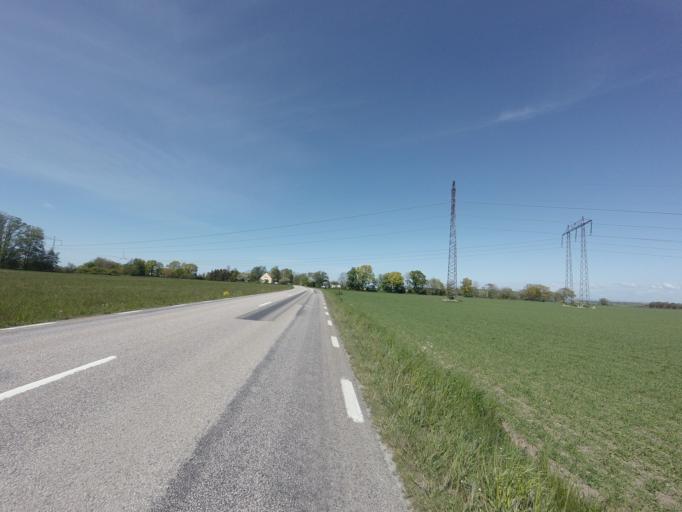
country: SE
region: Skane
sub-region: Helsingborg
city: Odakra
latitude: 56.1356
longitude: 12.6904
